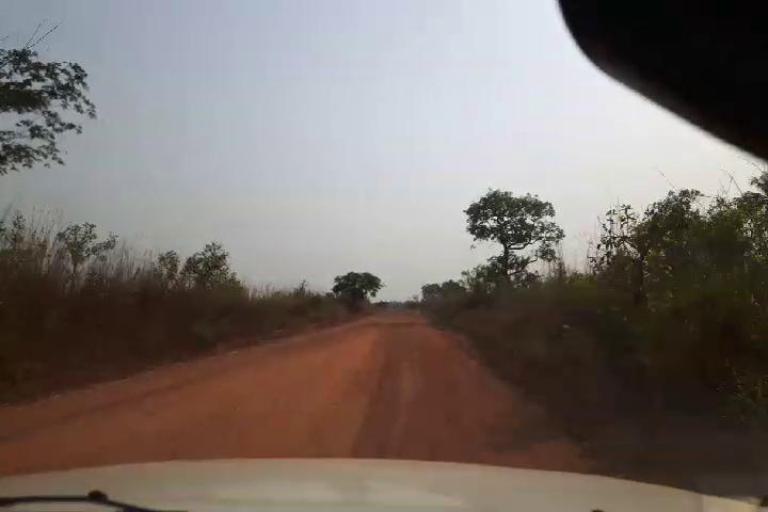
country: SL
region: Northern Province
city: Masingbi
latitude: 8.8027
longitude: -11.8638
